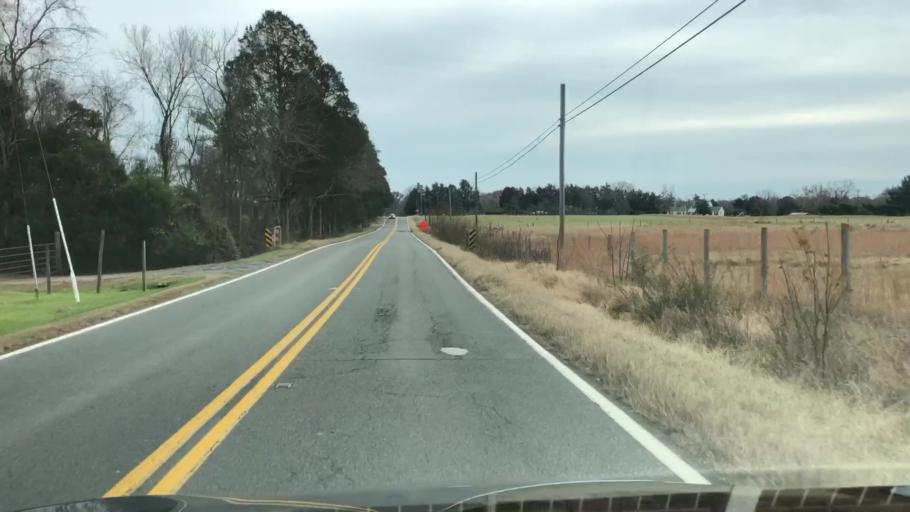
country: US
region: Virginia
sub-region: Fauquier County
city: New Baltimore
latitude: 38.7605
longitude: -77.6787
